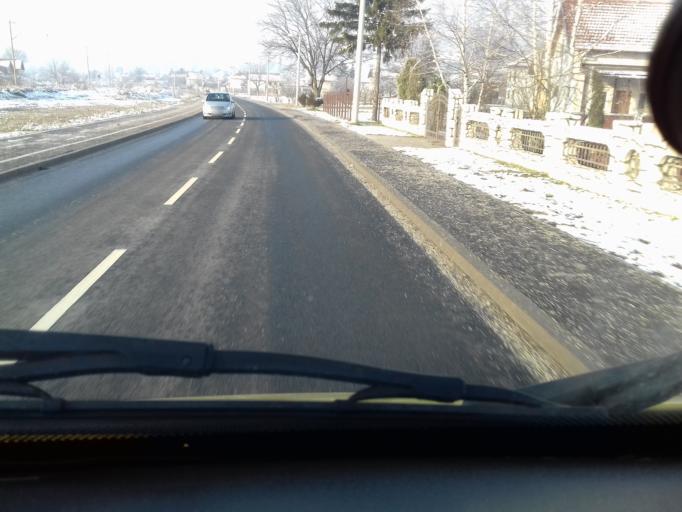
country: BA
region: Federation of Bosnia and Herzegovina
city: Mahala
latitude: 43.9838
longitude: 18.2385
